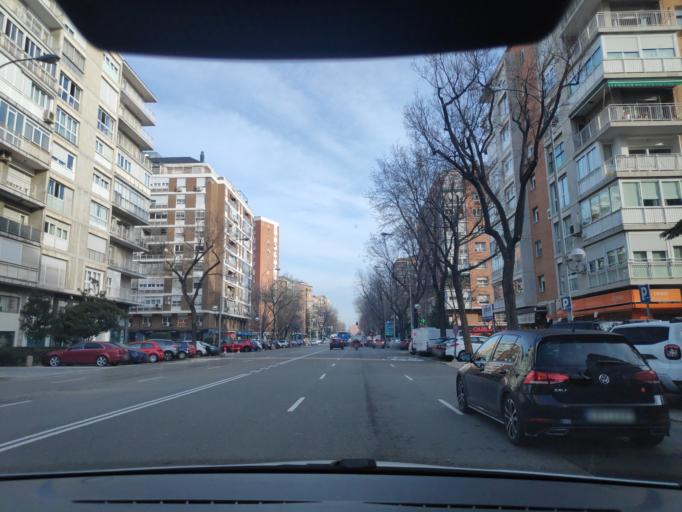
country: ES
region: Madrid
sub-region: Provincia de Madrid
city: Chamartin
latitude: 40.4504
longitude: -3.6776
